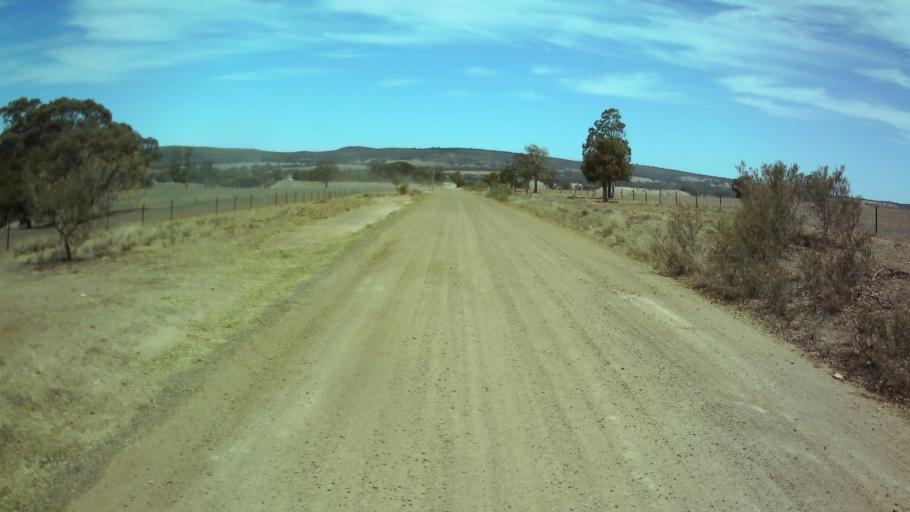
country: AU
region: New South Wales
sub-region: Weddin
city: Grenfell
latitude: -33.8229
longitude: 148.1688
